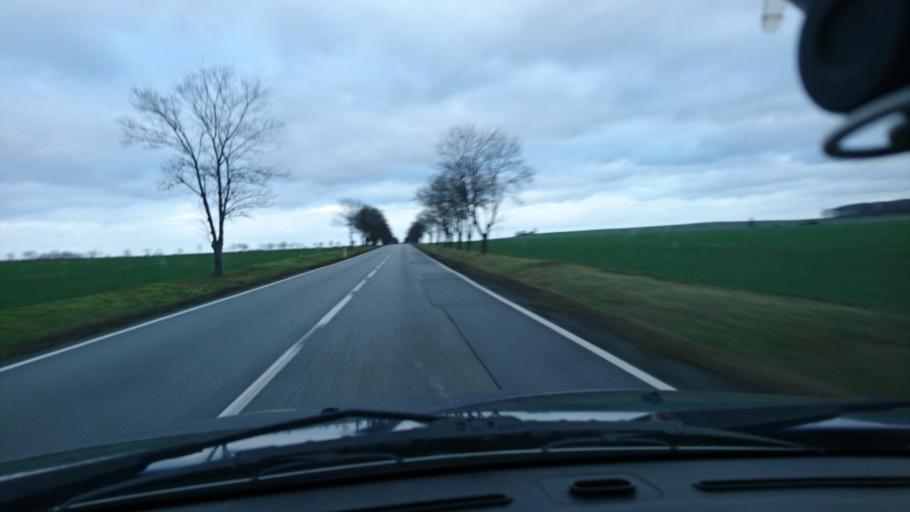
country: PL
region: Opole Voivodeship
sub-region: Powiat kluczborski
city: Byczyna
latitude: 51.0867
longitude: 18.1991
